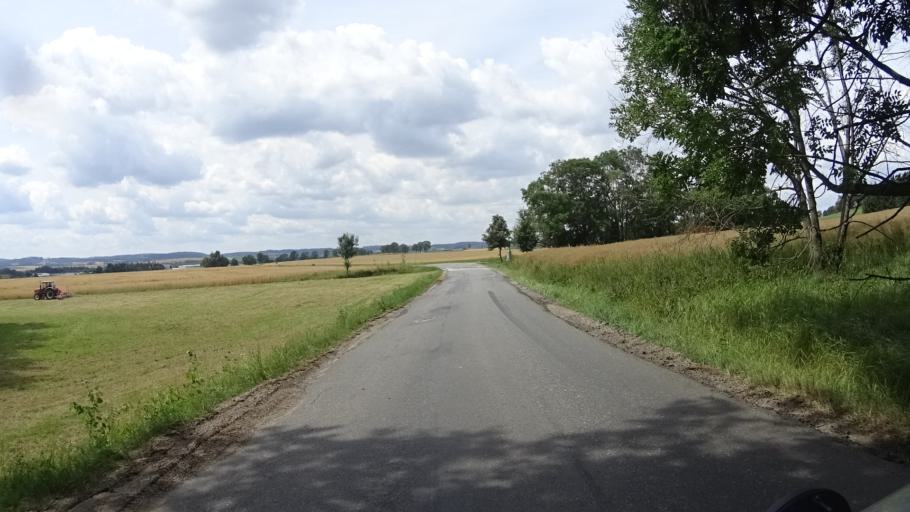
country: CZ
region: Vysocina
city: Merin
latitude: 49.4070
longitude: 15.9254
